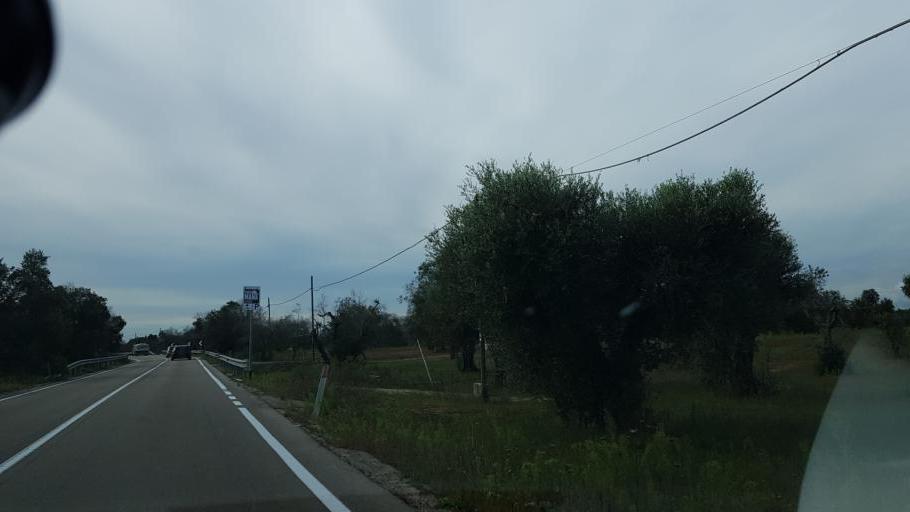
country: IT
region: Apulia
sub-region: Provincia di Lecce
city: Struda
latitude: 40.3607
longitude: 18.3151
